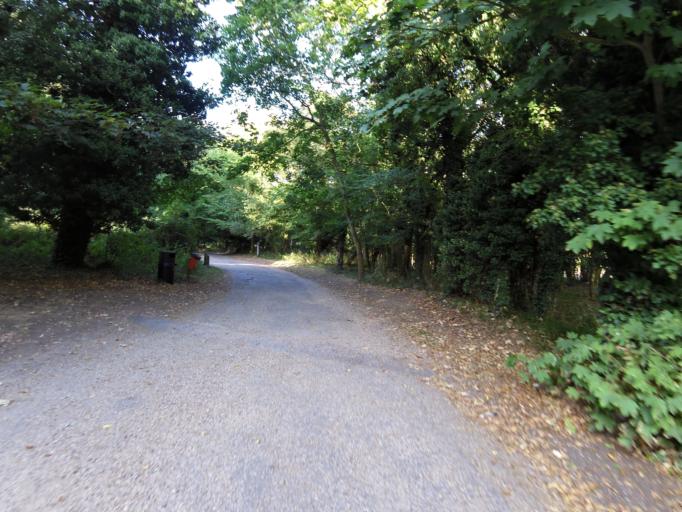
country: GB
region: England
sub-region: Suffolk
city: Kesgrave
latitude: 52.0065
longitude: 1.2331
